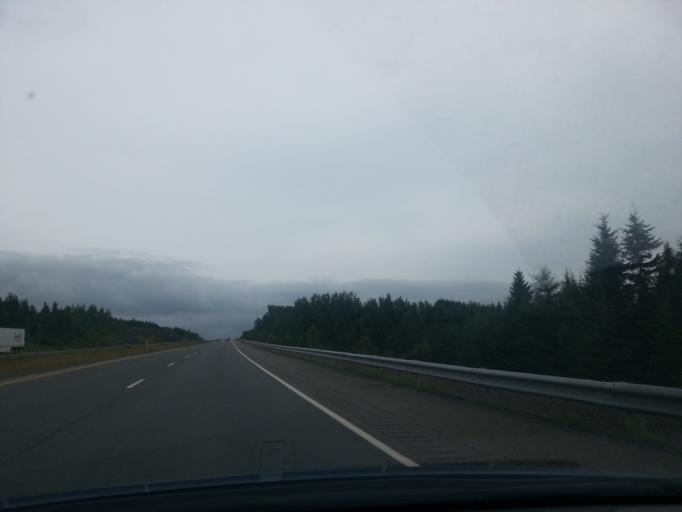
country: CA
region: New Brunswick
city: Harrison Brook
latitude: 47.2844
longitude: -68.0300
